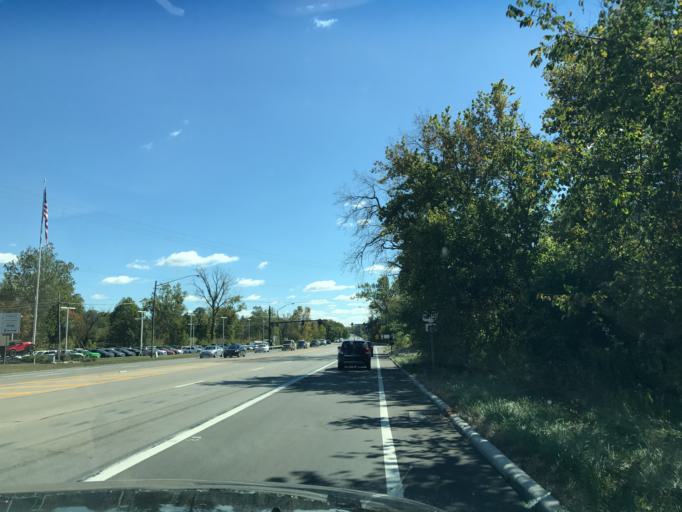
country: US
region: Ohio
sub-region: Delaware County
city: Delaware
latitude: 40.2571
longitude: -83.0641
